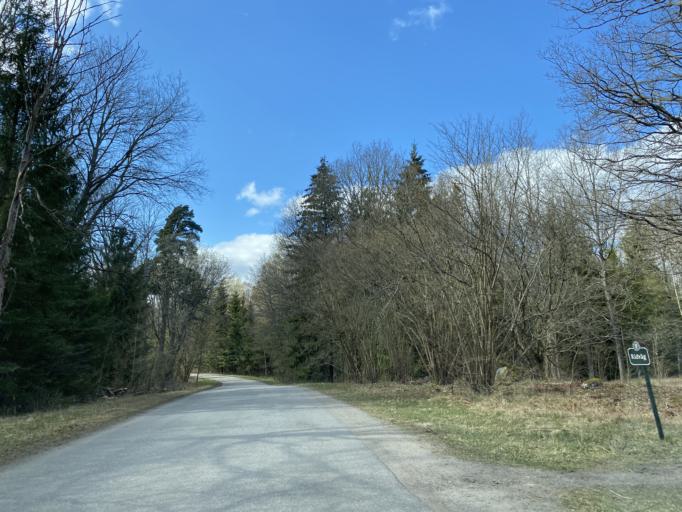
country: SE
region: Stockholm
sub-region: Nacka Kommun
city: Nacka
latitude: 59.3306
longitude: 18.1461
